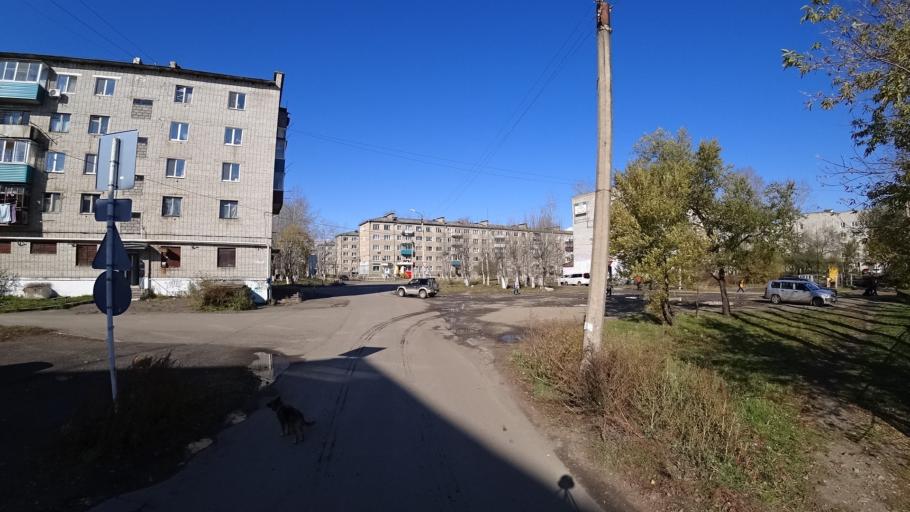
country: RU
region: Khabarovsk Krai
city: Amursk
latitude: 50.0984
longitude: 136.5133
